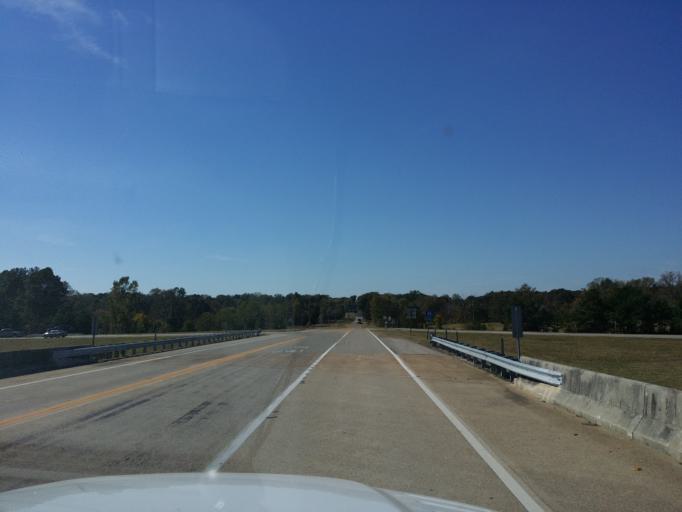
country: US
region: Mississippi
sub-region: Alcorn County
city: Corinth
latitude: 34.9819
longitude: -88.5212
